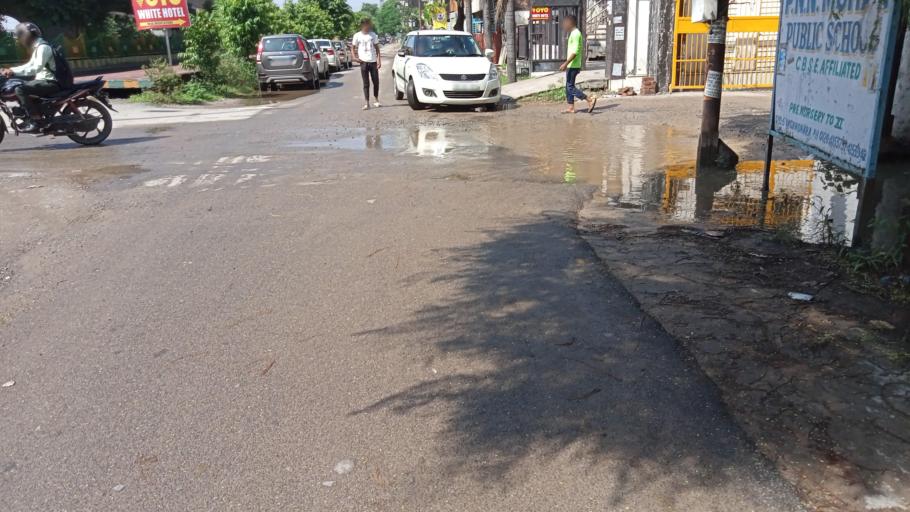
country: IN
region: Uttar Pradesh
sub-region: Ghaziabad
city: Ghaziabad
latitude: 28.6593
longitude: 77.3755
